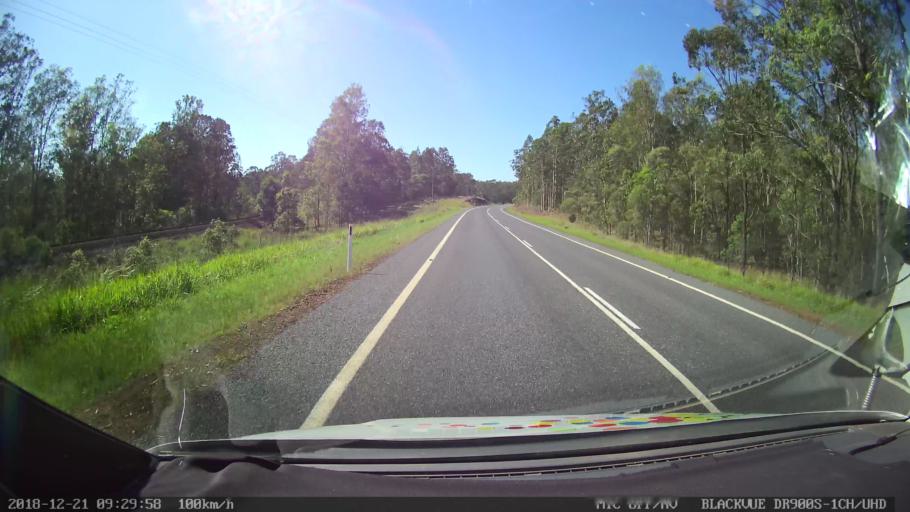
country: AU
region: New South Wales
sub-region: Clarence Valley
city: Maclean
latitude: -29.4395
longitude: 152.9911
